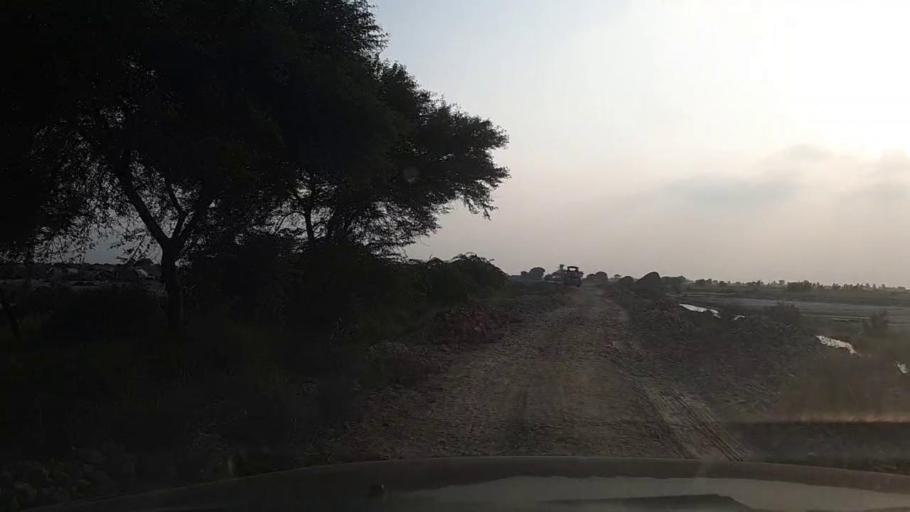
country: PK
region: Sindh
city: Jati
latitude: 24.5360
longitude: 68.3599
